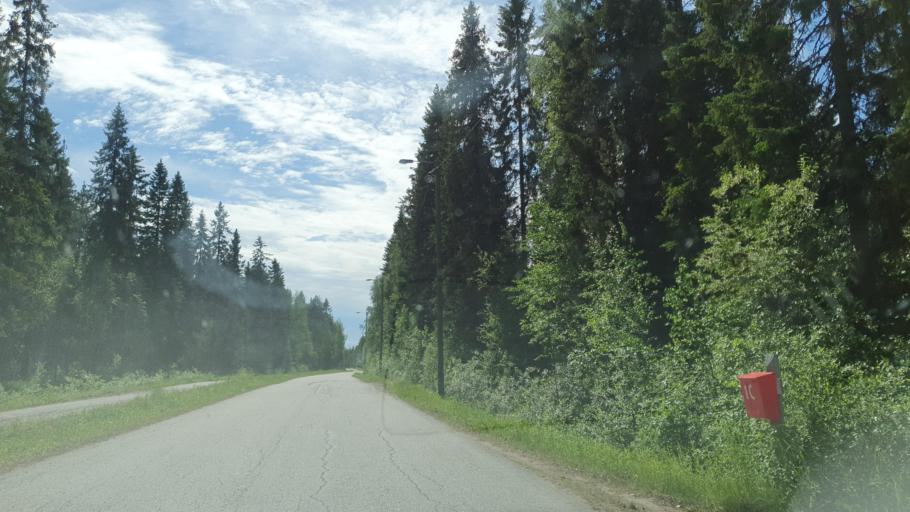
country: FI
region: Kainuu
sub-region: Kehys-Kainuu
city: Hyrynsalmi
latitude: 64.6856
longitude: 28.4658
